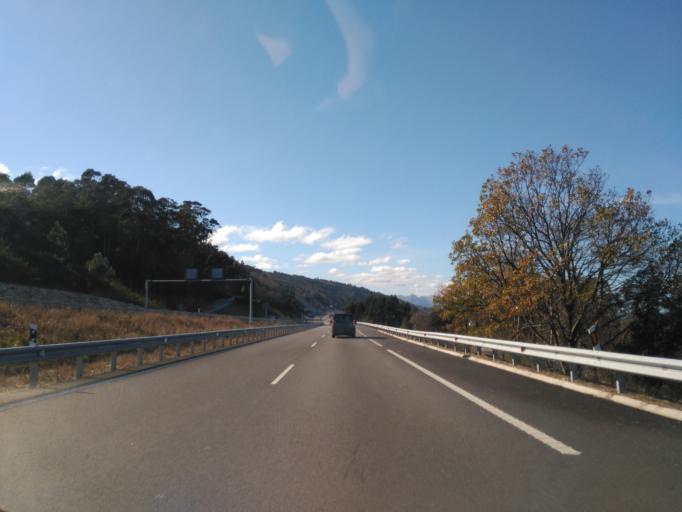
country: ES
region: Cantabria
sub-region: Provincia de Cantabria
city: Tresviso
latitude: 43.3930
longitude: -4.6022
